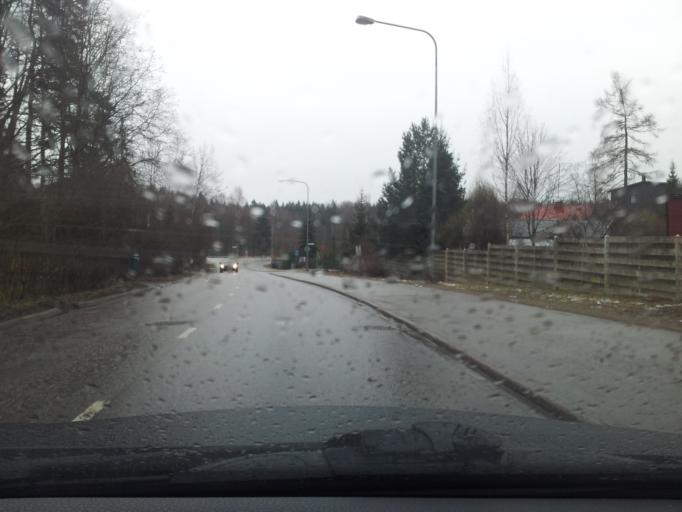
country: FI
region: Uusimaa
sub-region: Helsinki
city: Espoo
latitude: 60.1578
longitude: 24.6807
